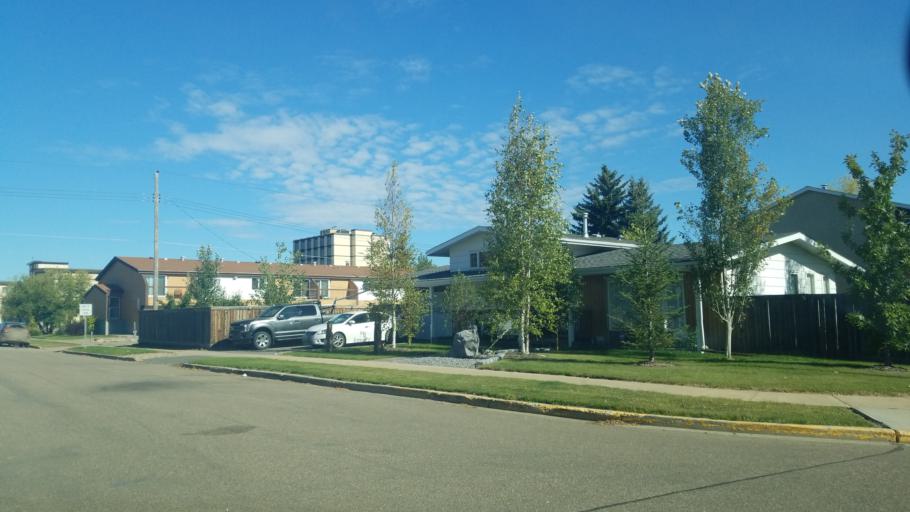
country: CA
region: Saskatchewan
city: Lloydminster
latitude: 53.2760
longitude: -110.0225
